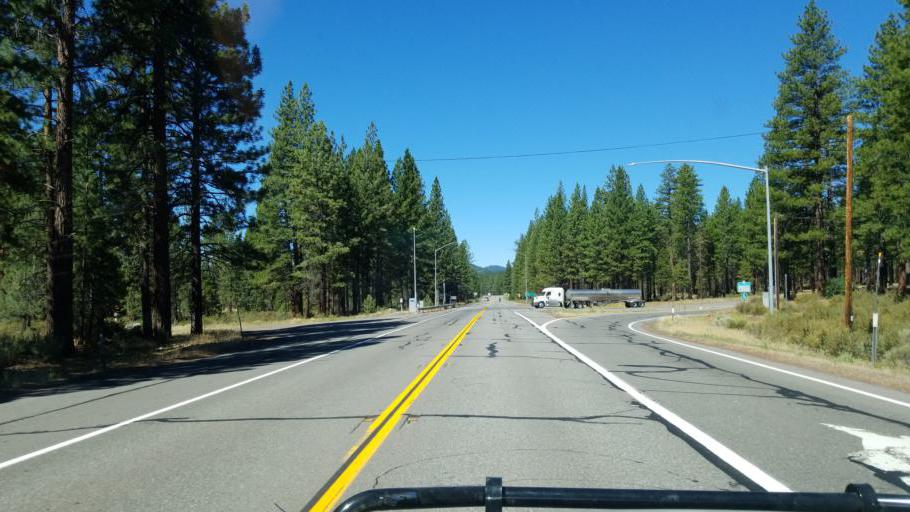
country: US
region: California
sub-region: Lassen County
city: Susanville
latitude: 40.4115
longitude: -120.7541
